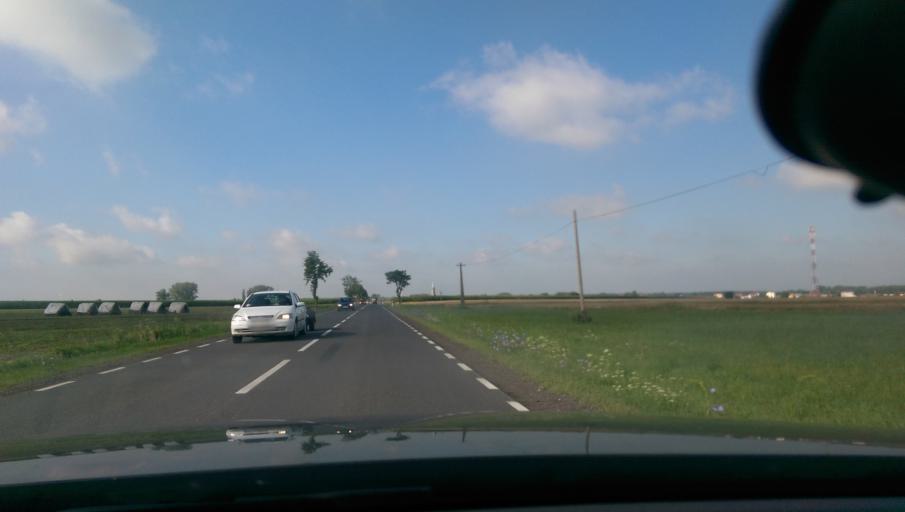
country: PL
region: Masovian Voivodeship
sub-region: Powiat plonski
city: Sochocin
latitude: 52.6985
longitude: 20.4826
